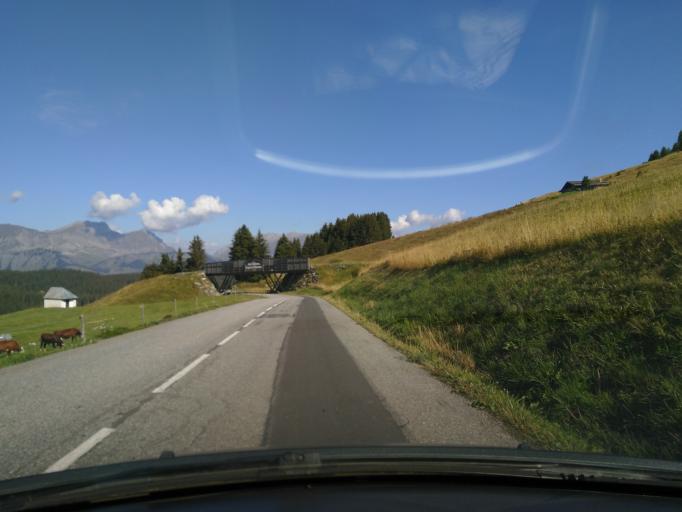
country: FR
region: Rhone-Alpes
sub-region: Departement de la Savoie
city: Beaufort
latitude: 45.7645
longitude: 6.5337
